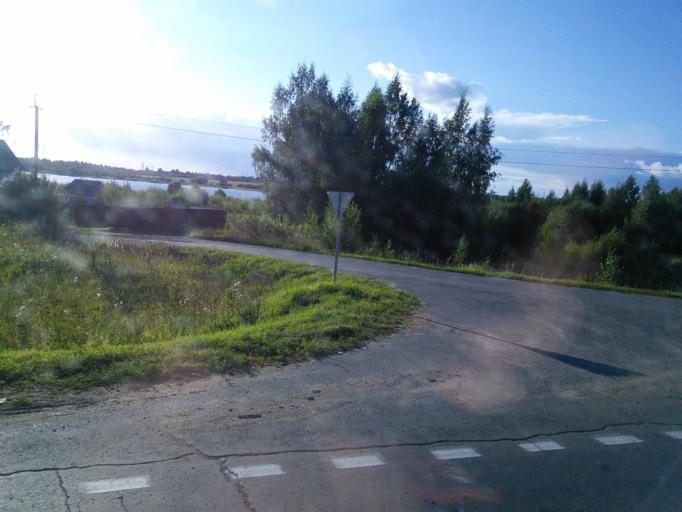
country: RU
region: Jaroslavl
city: Poshekhon'ye
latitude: 58.4923
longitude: 39.0902
